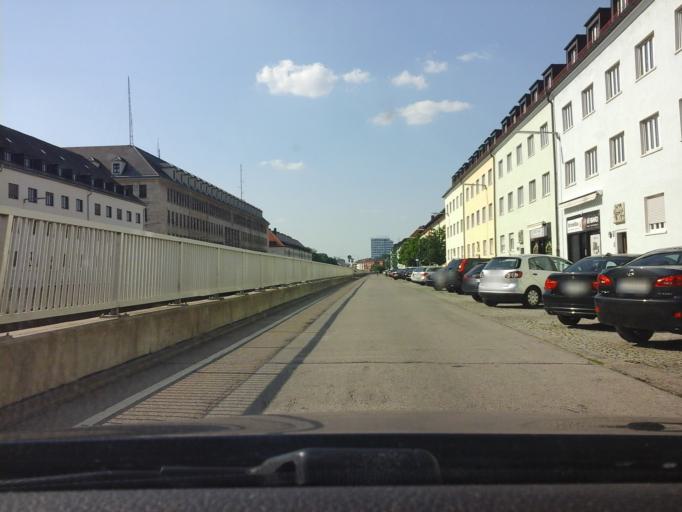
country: DE
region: Bavaria
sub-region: Upper Bavaria
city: Munich
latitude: 48.1008
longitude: 11.5846
